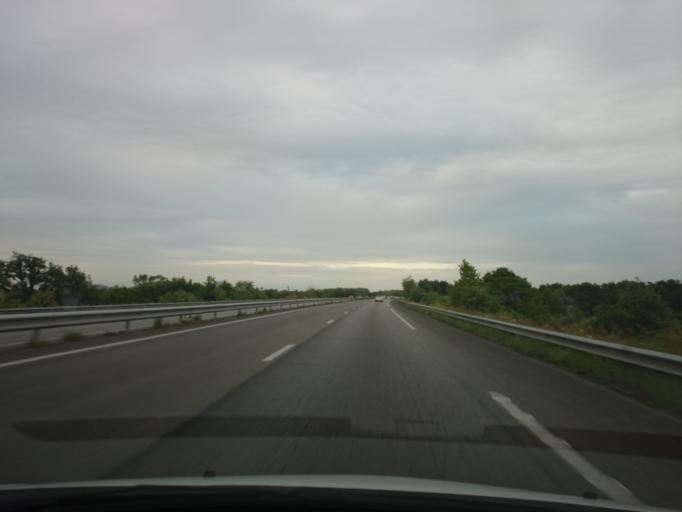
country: FR
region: Pays de la Loire
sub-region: Departement de la Loire-Atlantique
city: Heric
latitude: 47.4534
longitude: -1.6409
